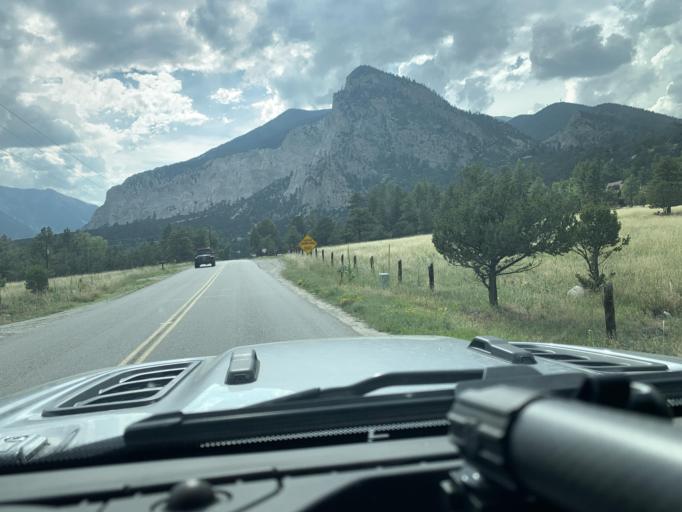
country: US
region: Colorado
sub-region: Chaffee County
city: Buena Vista
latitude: 38.7327
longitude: -106.1661
